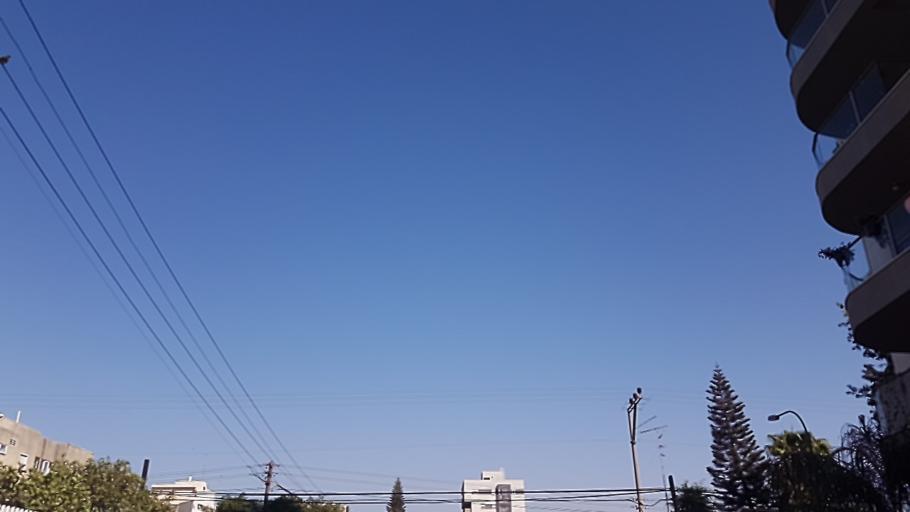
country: IL
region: Tel Aviv
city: Giv`atayim
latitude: 32.0673
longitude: 34.8240
